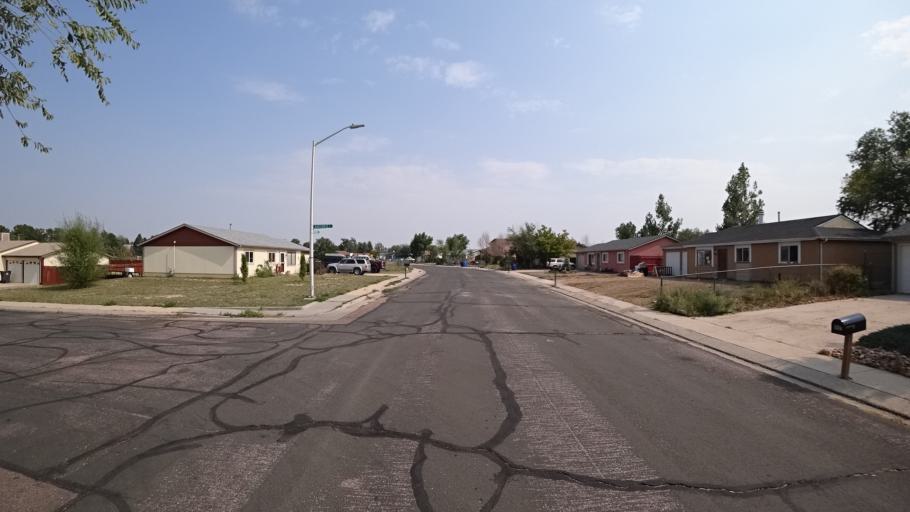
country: US
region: Colorado
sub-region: El Paso County
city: Cimarron Hills
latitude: 38.8320
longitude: -104.7448
